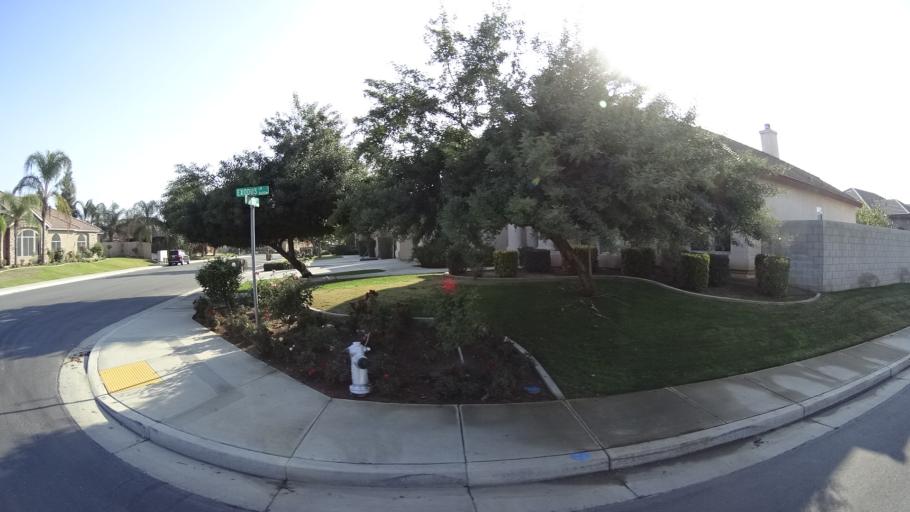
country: US
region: California
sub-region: Kern County
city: Greenacres
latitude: 35.4191
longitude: -119.0979
